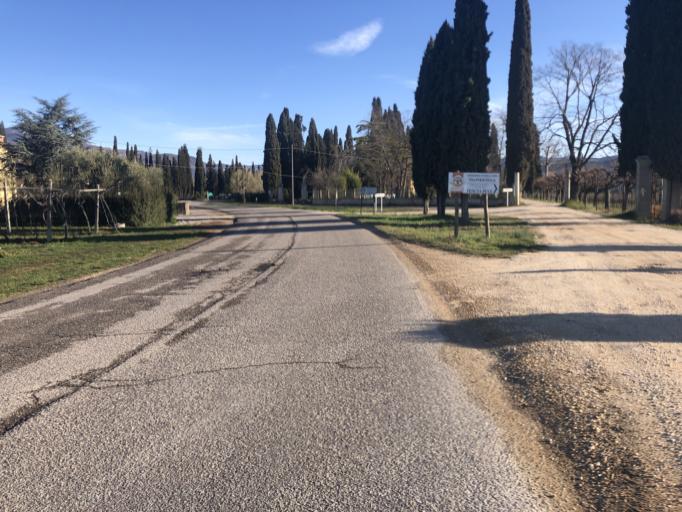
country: IT
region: Veneto
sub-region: Provincia di Verona
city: San Pietro in Cariano
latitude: 45.5054
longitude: 10.8837
